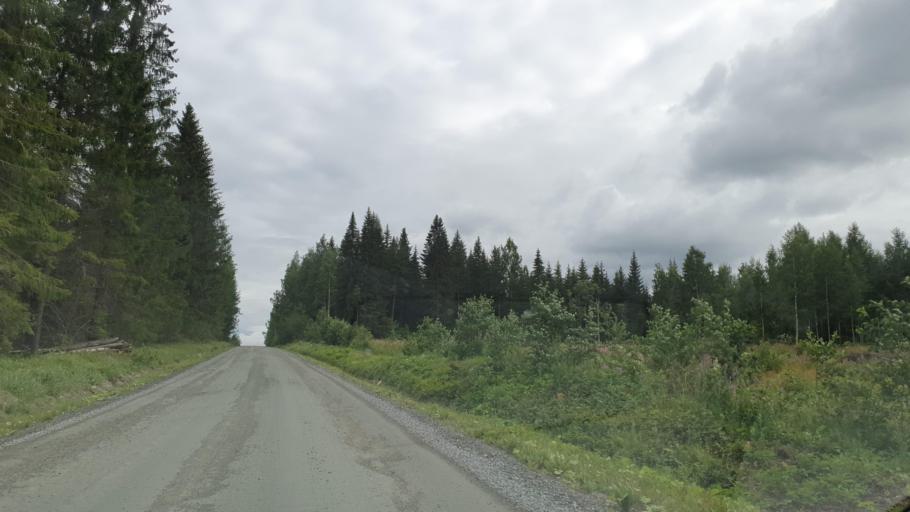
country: FI
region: Northern Savo
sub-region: Ylae-Savo
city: Iisalmi
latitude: 63.5263
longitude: 27.0897
